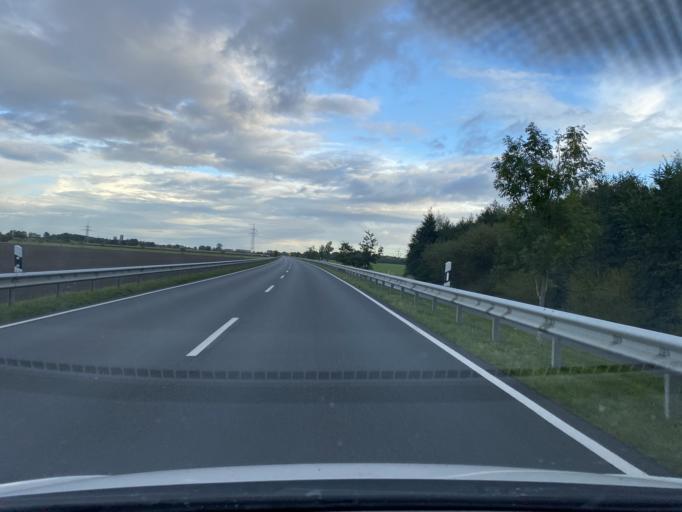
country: DE
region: Lower Saxony
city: Otterndorf
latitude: 53.7968
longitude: 8.8787
